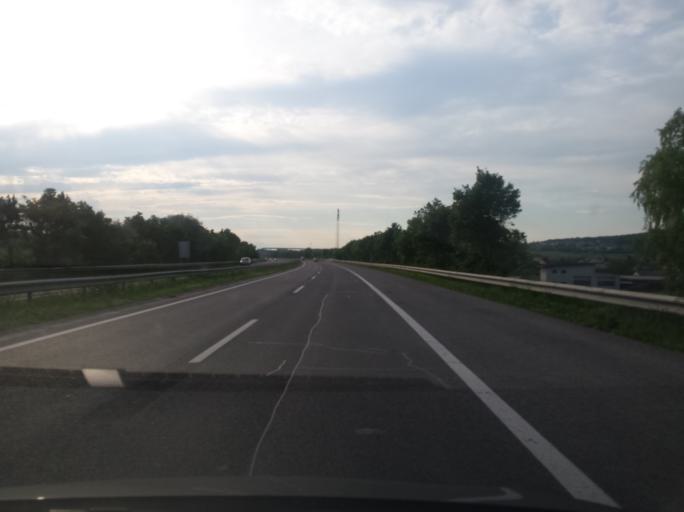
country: AT
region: Burgenland
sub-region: Eisenstadt-Umgebung
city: Mullendorf
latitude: 47.8233
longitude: 16.4851
